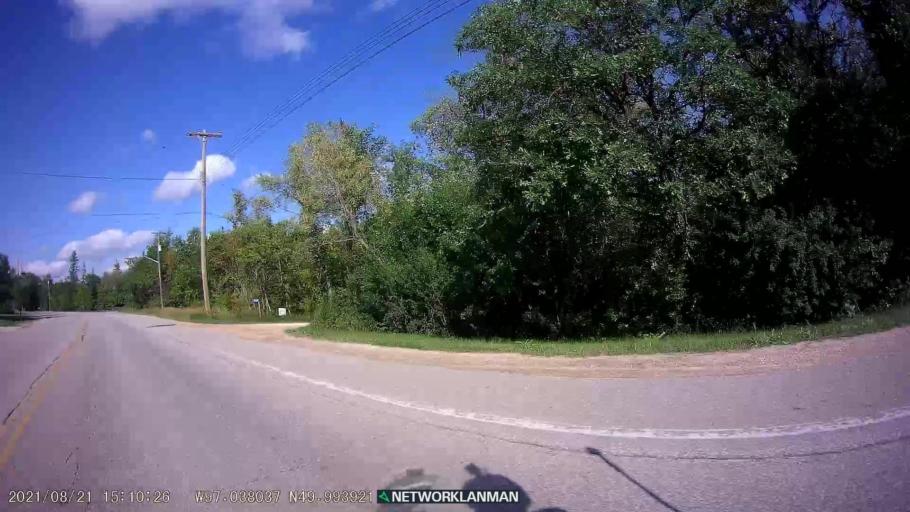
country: CA
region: Manitoba
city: Winnipeg
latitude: 49.9941
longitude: -97.0380
